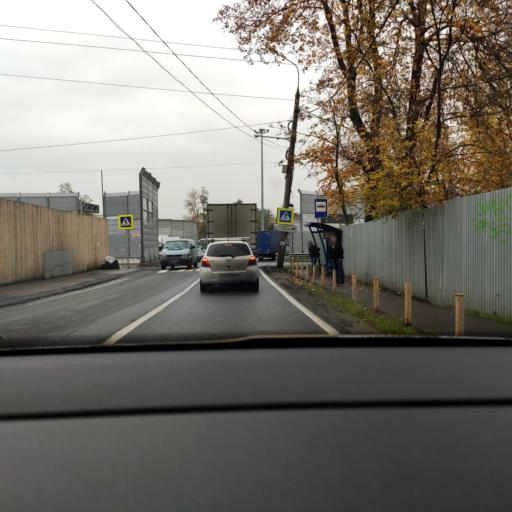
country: RU
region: Moskovskaya
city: Druzhba
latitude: 55.8873
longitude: 37.7383
